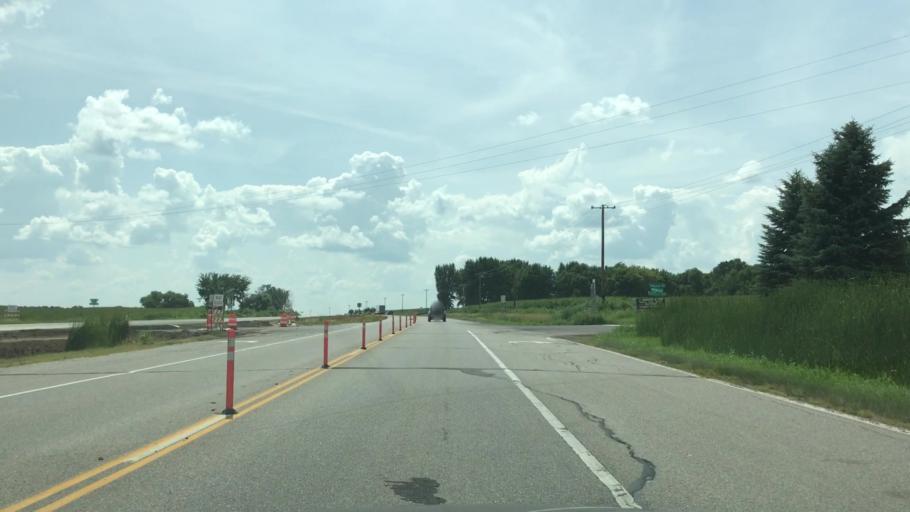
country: US
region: Minnesota
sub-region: Scott County
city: Belle Plaine
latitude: 44.5868
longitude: -93.8287
